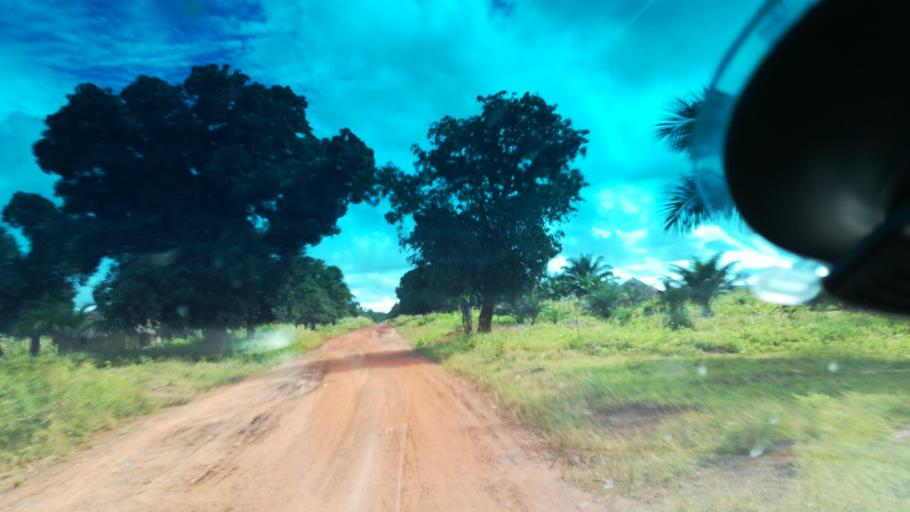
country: ZM
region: Luapula
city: Nchelenge
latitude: -9.1664
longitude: 28.2816
